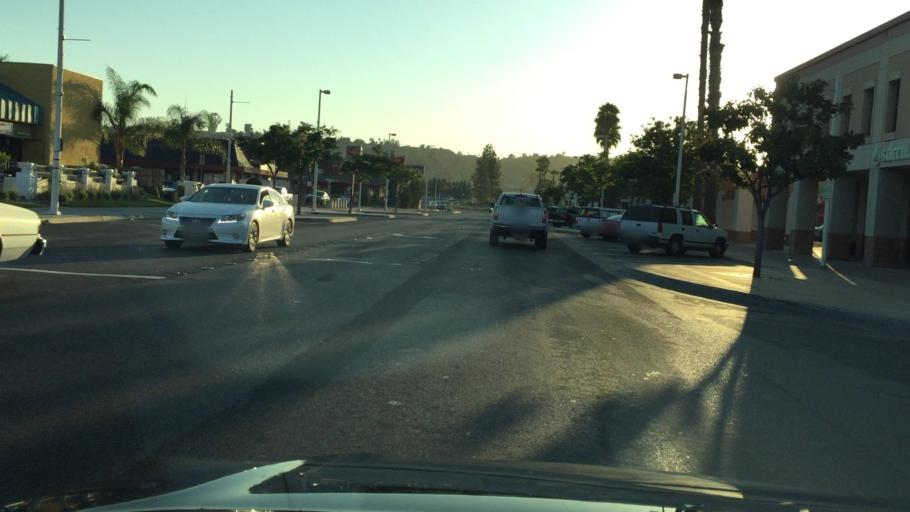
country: US
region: California
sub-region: San Diego County
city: El Cajon
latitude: 32.7950
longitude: -116.9649
